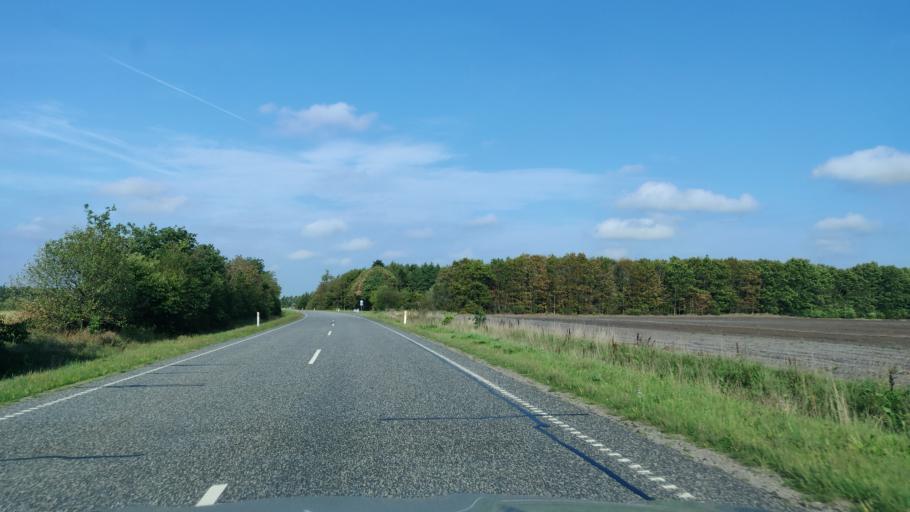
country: DK
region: Central Jutland
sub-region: Herning Kommune
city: Sunds
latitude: 56.2431
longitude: 9.0842
